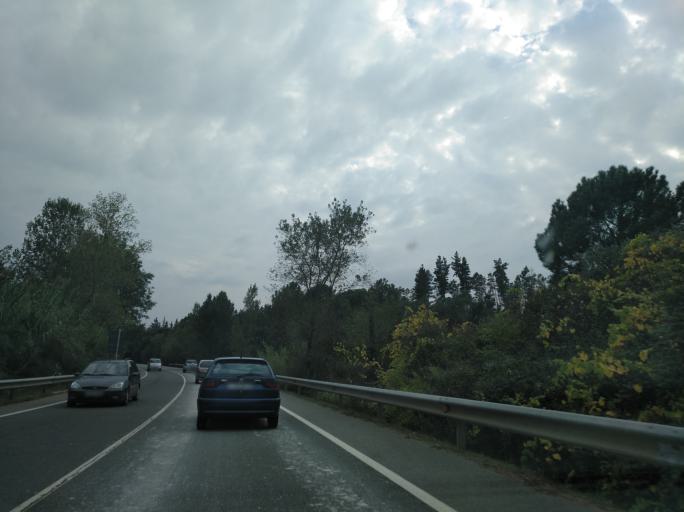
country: ES
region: Catalonia
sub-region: Provincia de Girona
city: Santa Coloma de Farners
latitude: 41.8786
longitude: 2.6579
